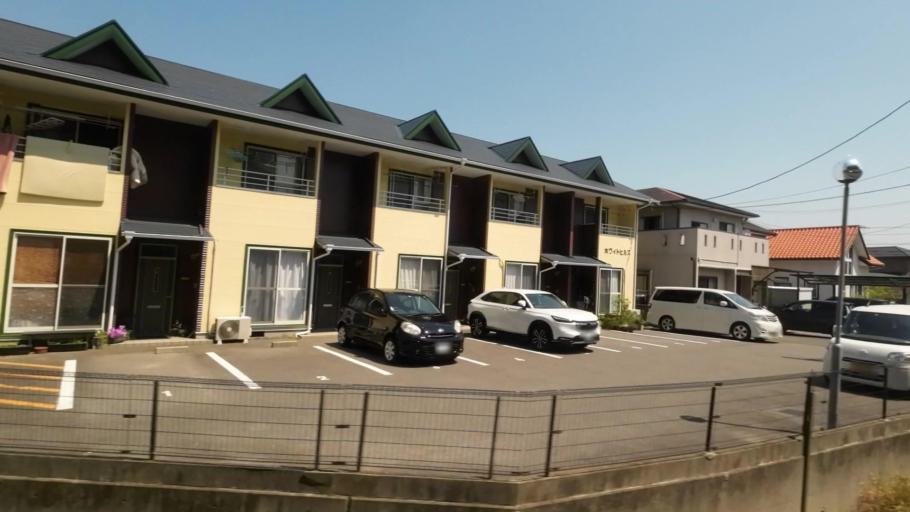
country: JP
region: Ehime
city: Hojo
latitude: 34.0962
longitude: 132.9541
